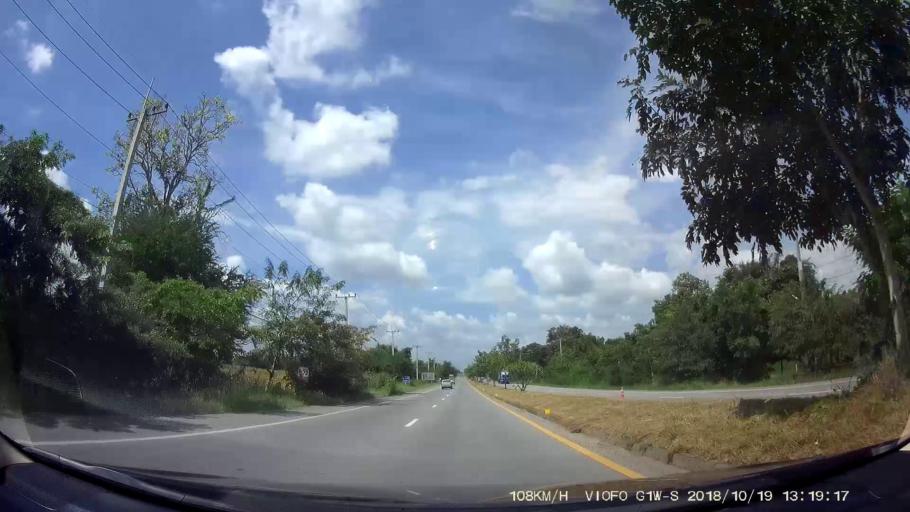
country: TH
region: Chaiyaphum
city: Chatturat
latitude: 15.4273
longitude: 101.8314
